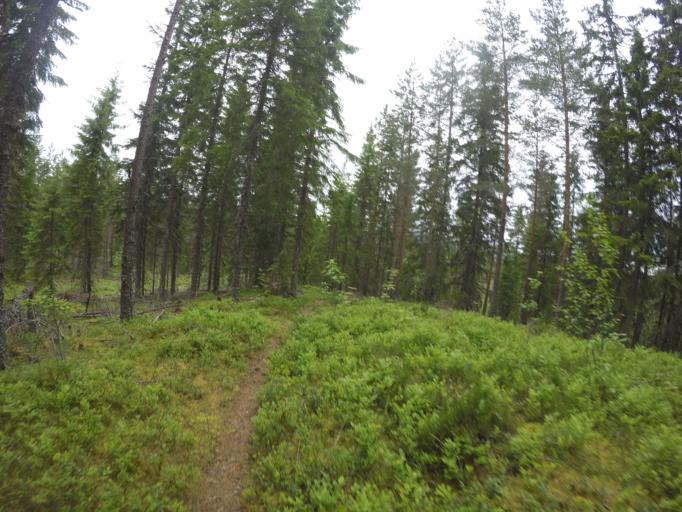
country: SE
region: Dalarna
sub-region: Ludvika Kommun
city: Abborrberget
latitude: 60.0768
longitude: 14.5242
